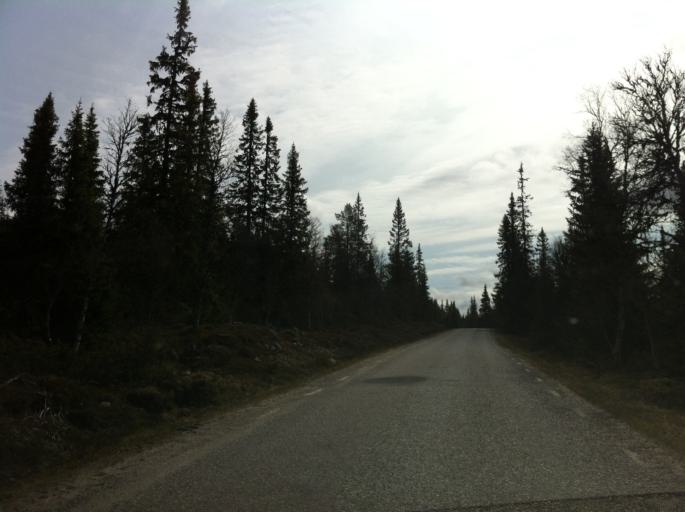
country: NO
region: Hedmark
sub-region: Engerdal
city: Engerdal
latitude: 62.3059
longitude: 12.8040
